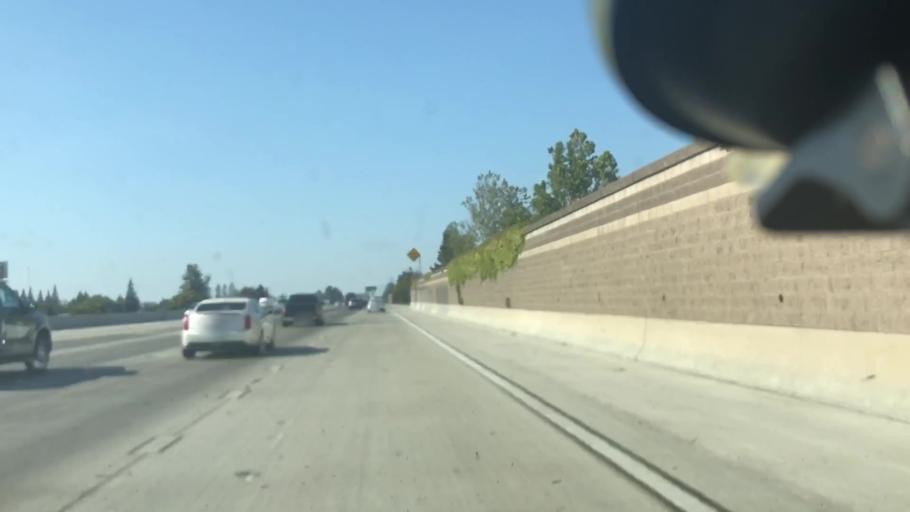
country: US
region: California
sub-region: San Joaquin County
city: Country Club
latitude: 37.9776
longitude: -121.3405
